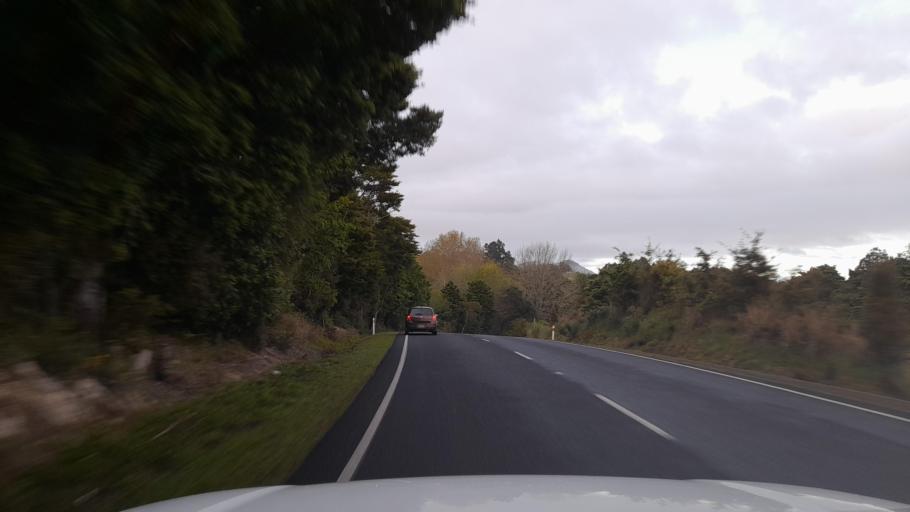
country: NZ
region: Northland
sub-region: Whangarei
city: Maungatapere
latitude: -35.7096
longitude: 174.0056
